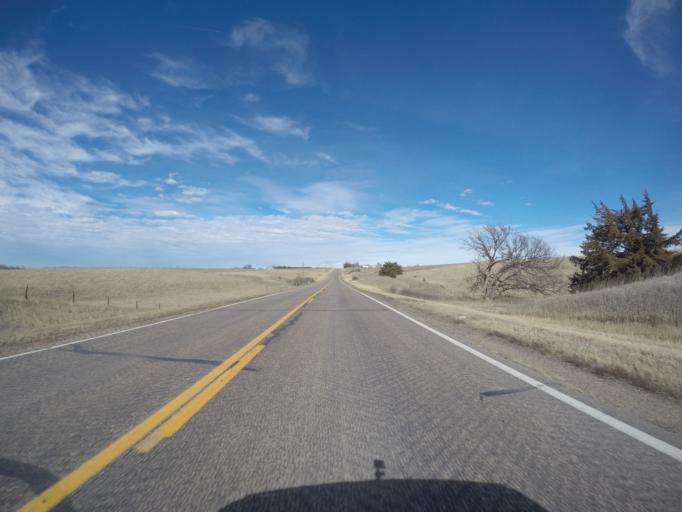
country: US
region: Nebraska
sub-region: Franklin County
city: Franklin
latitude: 40.1601
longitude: -98.9527
